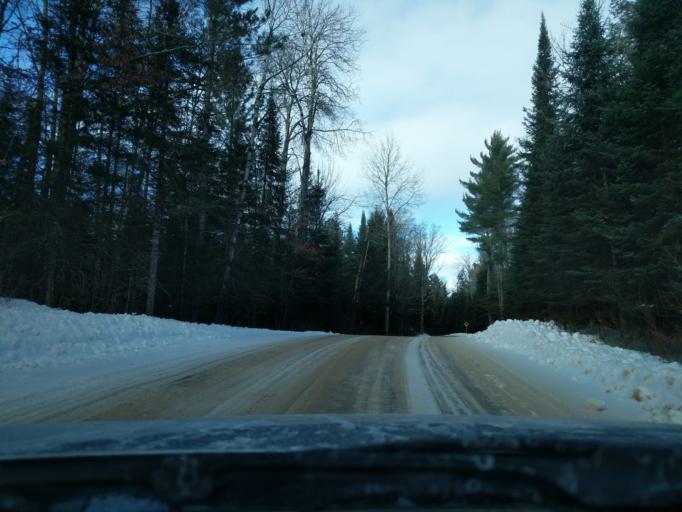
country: US
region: Wisconsin
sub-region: Vilas County
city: Eagle River
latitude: 45.8052
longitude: -89.0706
